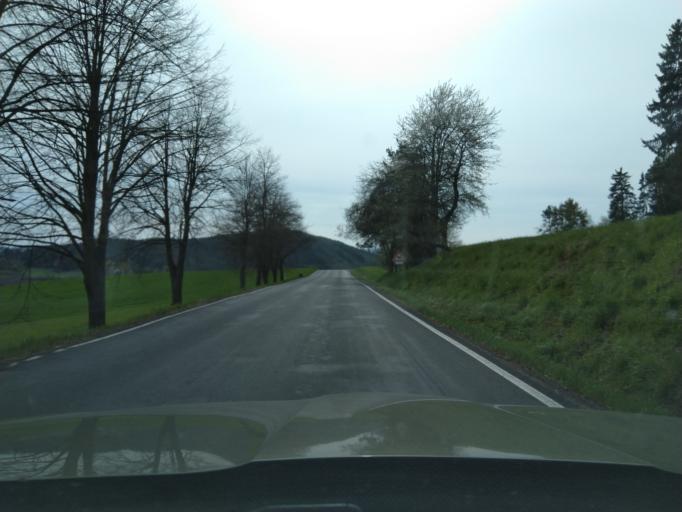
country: CZ
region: Plzensky
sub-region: Okres Klatovy
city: Susice
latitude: 49.2446
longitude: 13.5743
